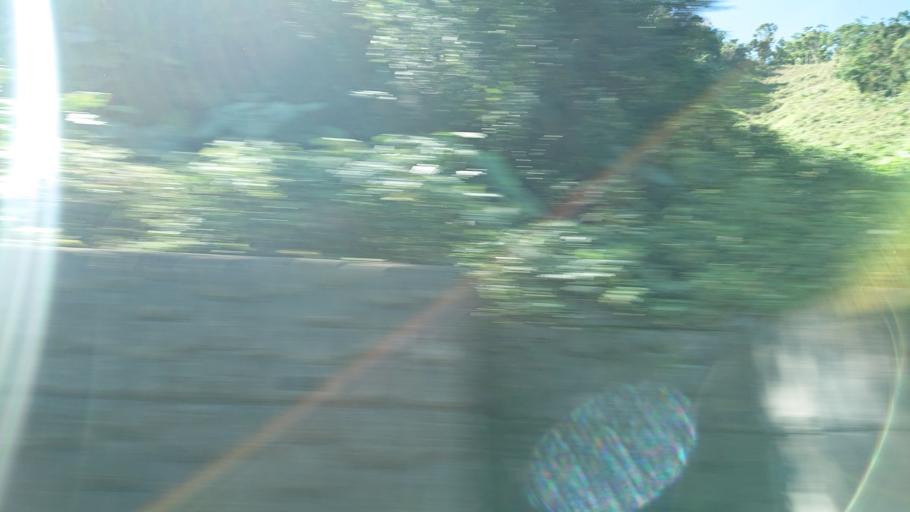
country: TW
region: Taiwan
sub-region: Yilan
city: Yilan
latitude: 24.5780
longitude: 121.4894
